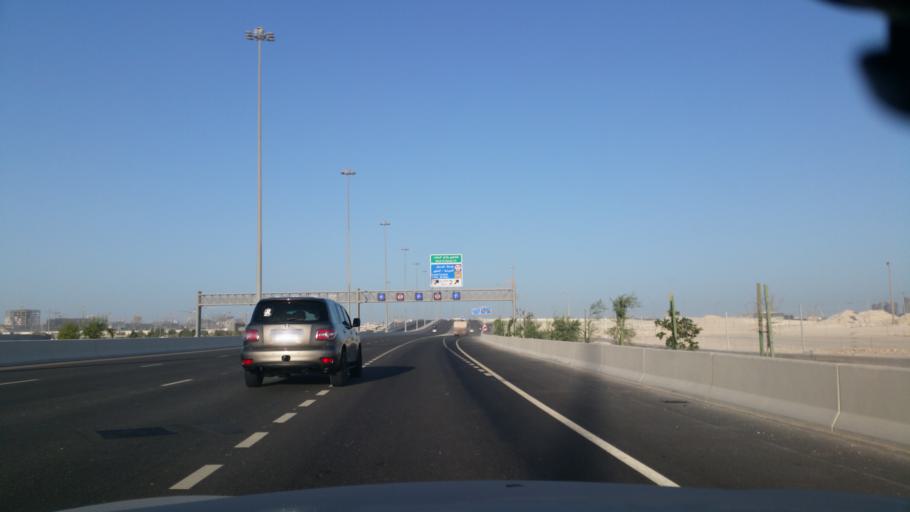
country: QA
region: Baladiyat Umm Salal
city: Umm Salal Muhammad
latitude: 25.4004
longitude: 51.4829
